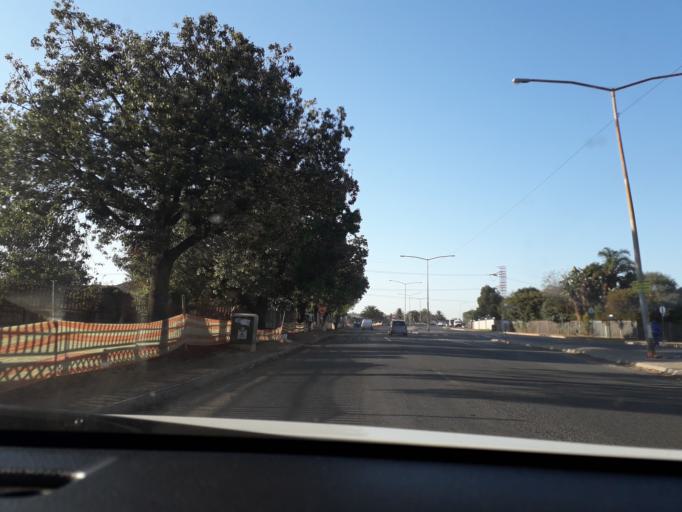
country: ZA
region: Gauteng
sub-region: City of Johannesburg Metropolitan Municipality
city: Modderfontein
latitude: -26.0649
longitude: 28.2071
